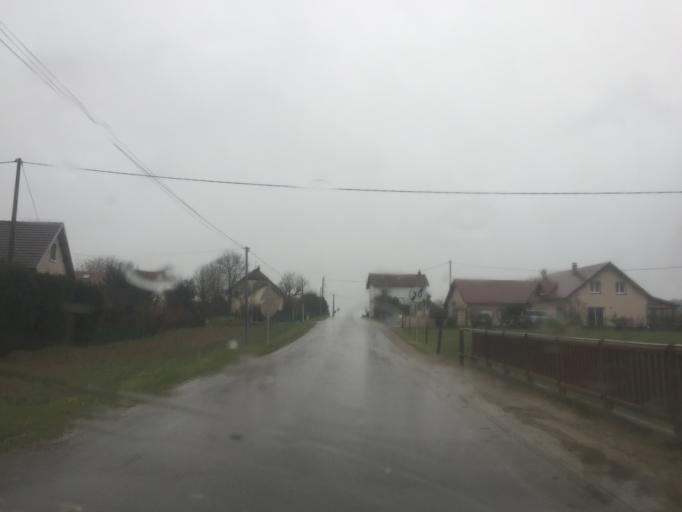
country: FR
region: Franche-Comte
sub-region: Departement du Jura
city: Dampierre
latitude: 47.2258
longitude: 5.7088
